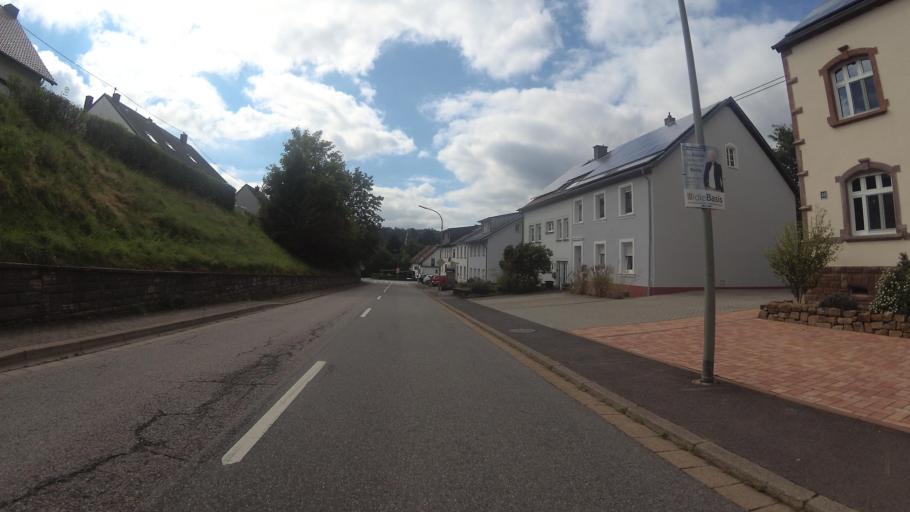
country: DE
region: Saarland
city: Grossrosseln
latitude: 49.1774
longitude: 6.8123
